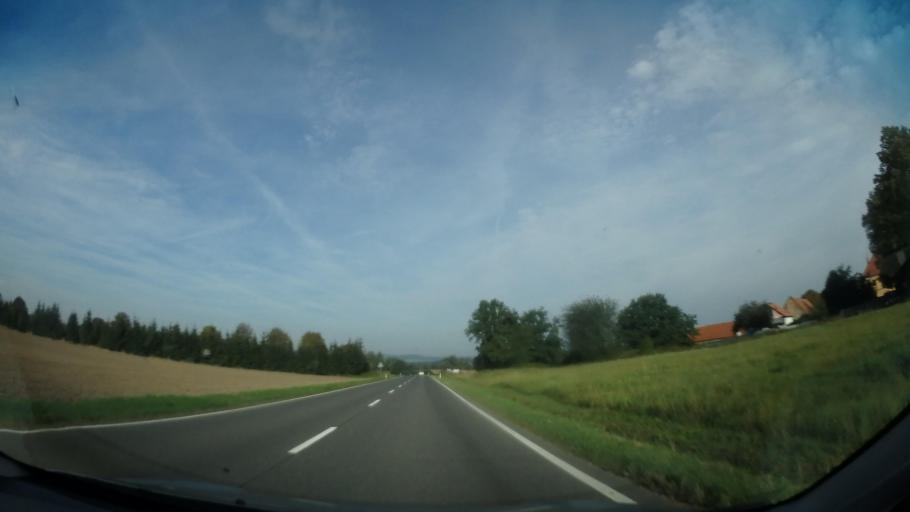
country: CZ
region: Jihocesky
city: Cimelice
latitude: 49.4367
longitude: 14.1425
